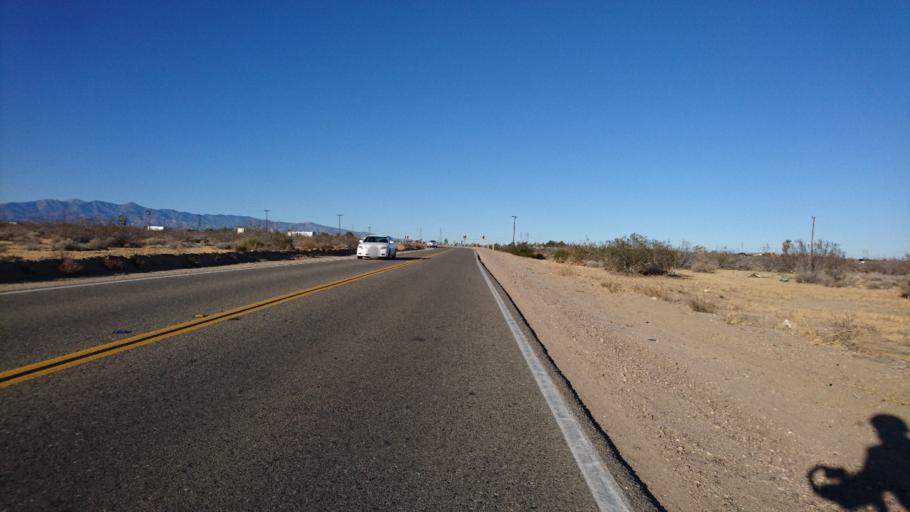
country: US
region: California
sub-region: San Bernardino County
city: Mountain View Acres
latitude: 34.4544
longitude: -117.3562
